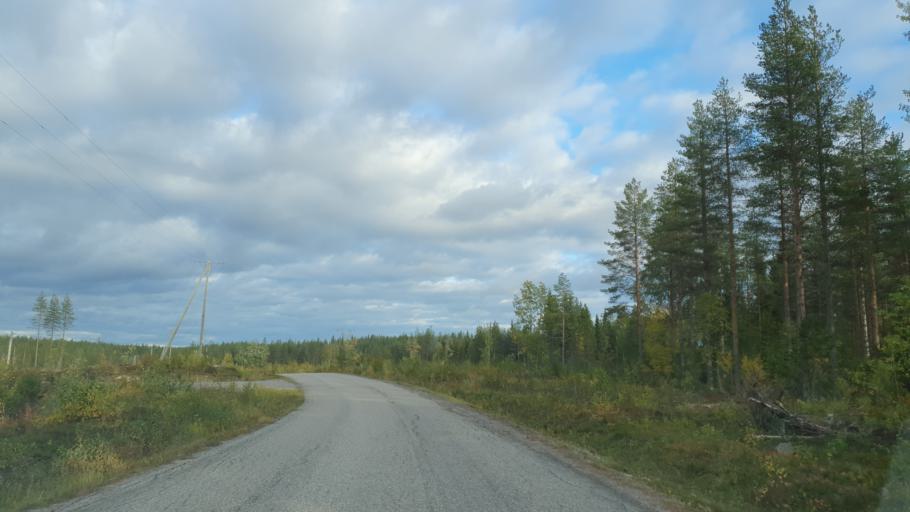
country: FI
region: North Karelia
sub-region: Pielisen Karjala
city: Lieksa
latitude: 63.9159
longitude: 30.1068
